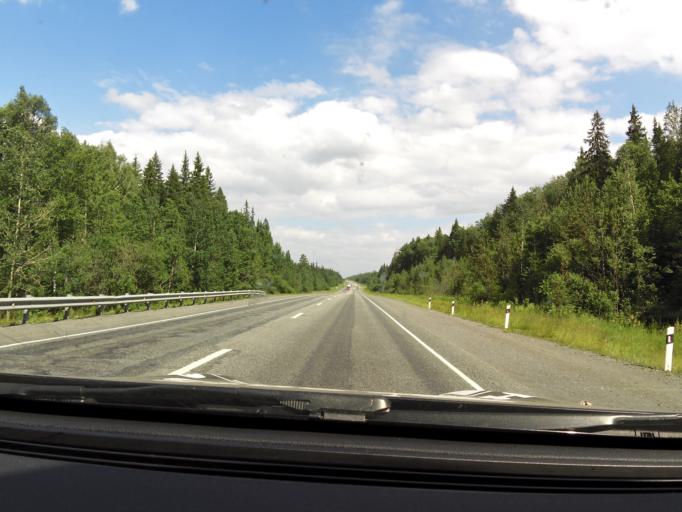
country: RU
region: Sverdlovsk
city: Bisert'
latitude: 56.8267
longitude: 59.2174
